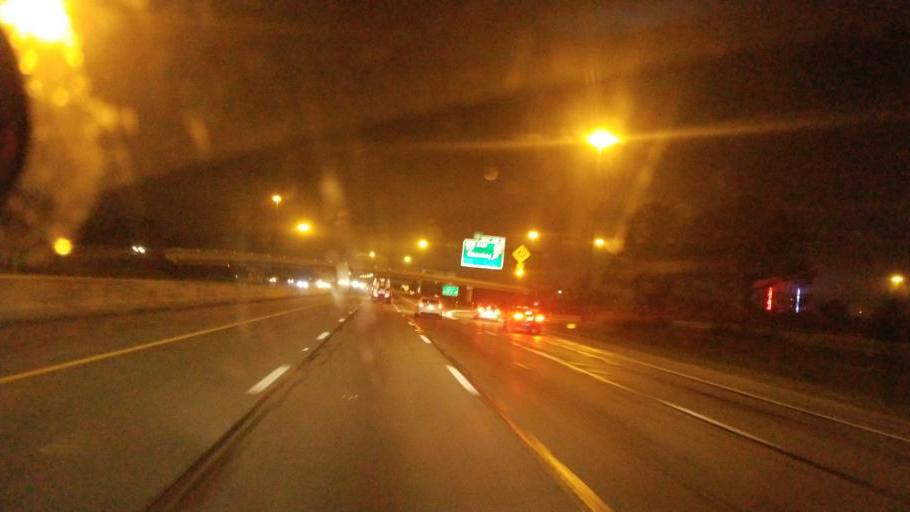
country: US
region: Ohio
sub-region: Franklin County
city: Worthington
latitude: 40.1100
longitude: -82.9781
